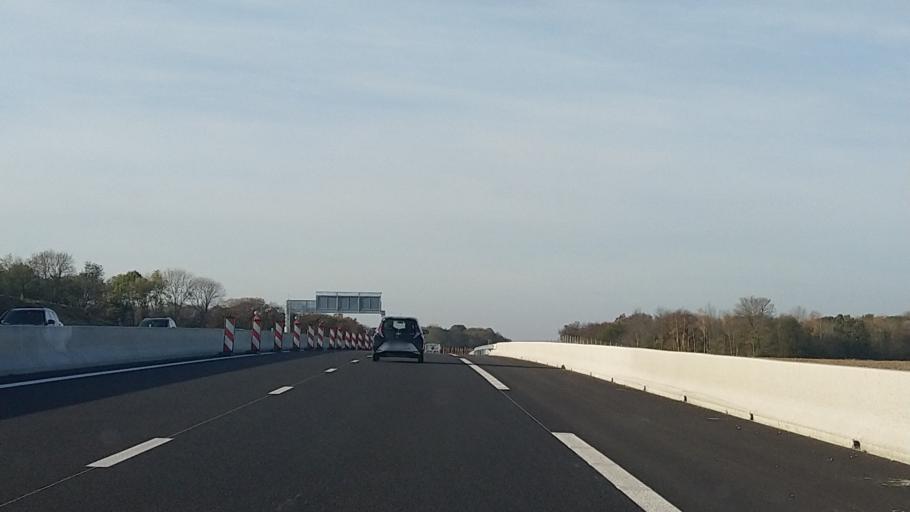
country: FR
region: Ile-de-France
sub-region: Departement du Val-d'Oise
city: Maffliers
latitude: 49.0882
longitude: 2.3129
